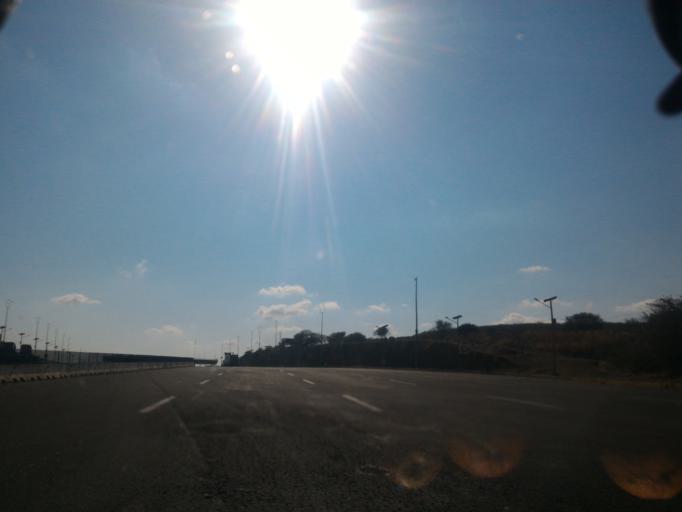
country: MX
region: Jalisco
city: Tonila
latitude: 19.4113
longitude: -103.5255
